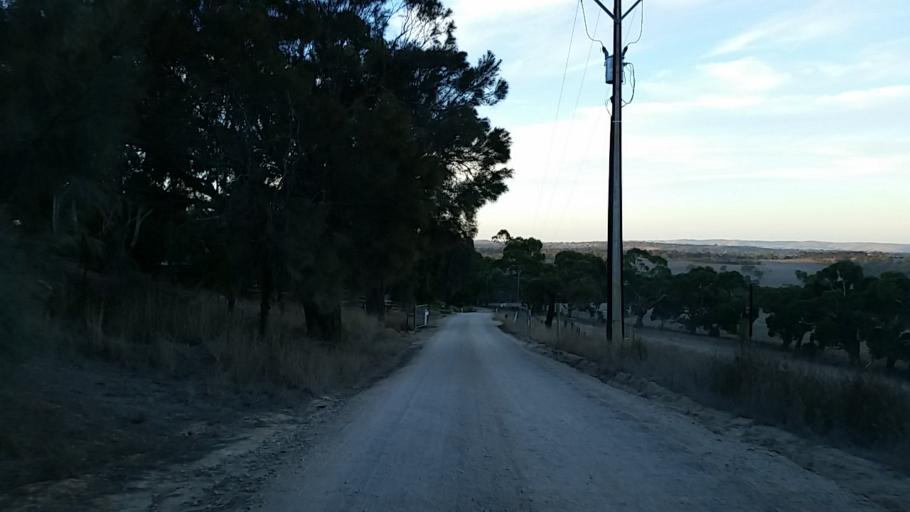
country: AU
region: South Australia
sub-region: Mount Barker
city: Nairne
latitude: -35.0618
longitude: 138.9244
